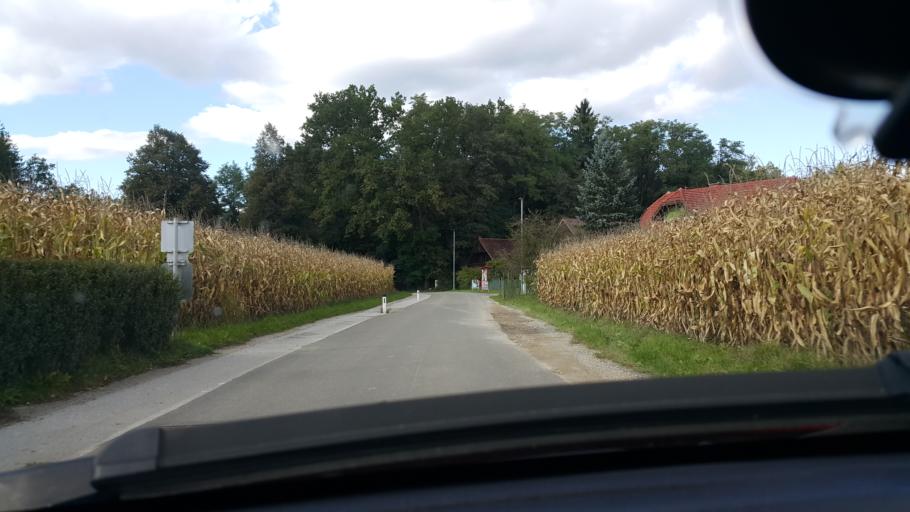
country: AT
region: Styria
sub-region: Politischer Bezirk Deutschlandsberg
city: Sankt Martin im Sulmtal
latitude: 46.7334
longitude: 15.2945
